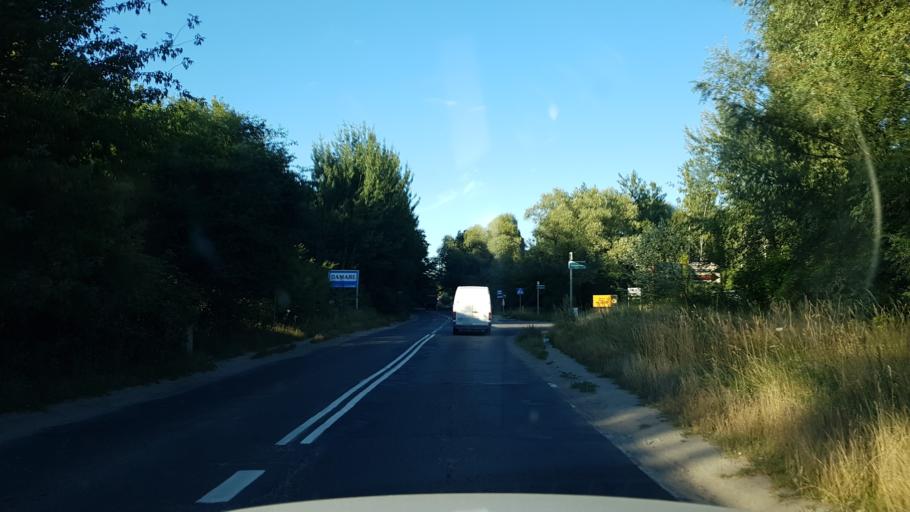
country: PL
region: West Pomeranian Voivodeship
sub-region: Szczecin
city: Szczecin
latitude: 53.3997
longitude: 14.5326
